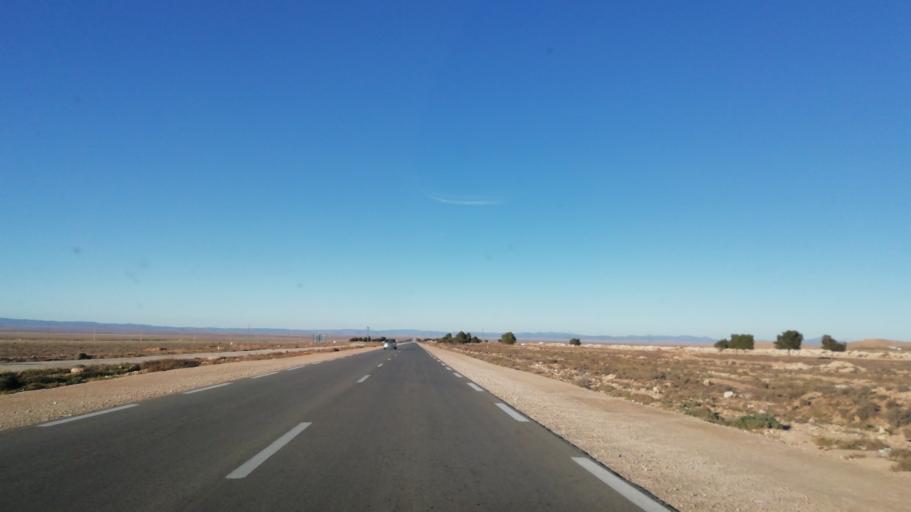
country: DZ
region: Tlemcen
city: Sebdou
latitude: 34.3024
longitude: -1.2614
